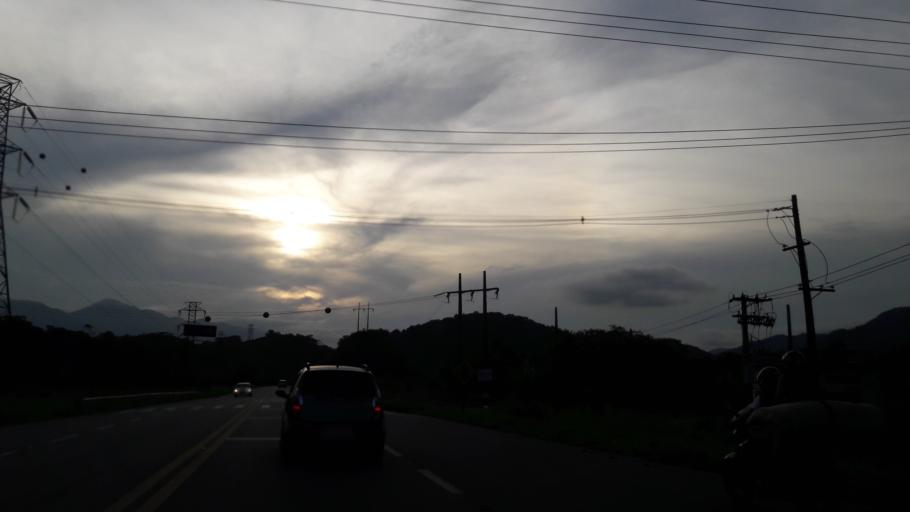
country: BR
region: Sao Paulo
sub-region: Peruibe
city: Peruibe
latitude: -24.2942
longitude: -47.0338
